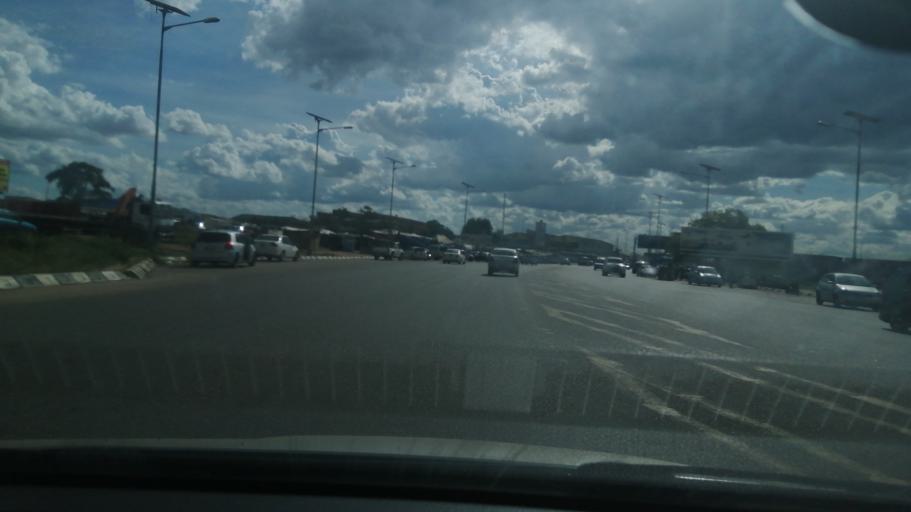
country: ZW
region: Harare
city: Harare
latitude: -17.8518
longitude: 31.0556
